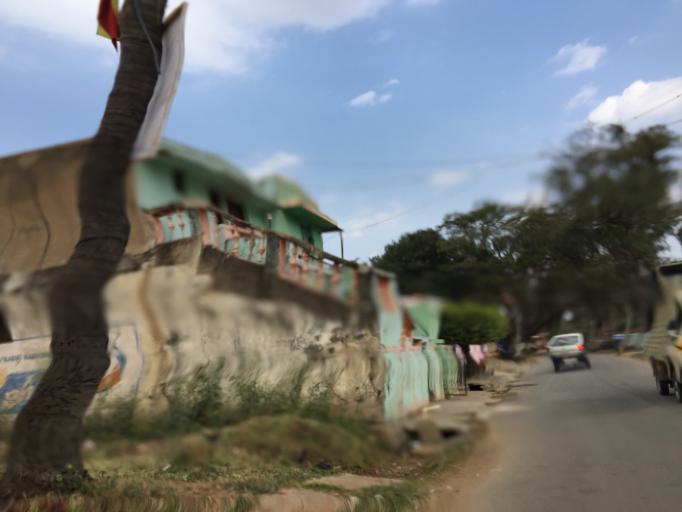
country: IN
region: Karnataka
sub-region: Chikkaballapur
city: Chik Ballapur
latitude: 13.3840
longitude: 77.6853
